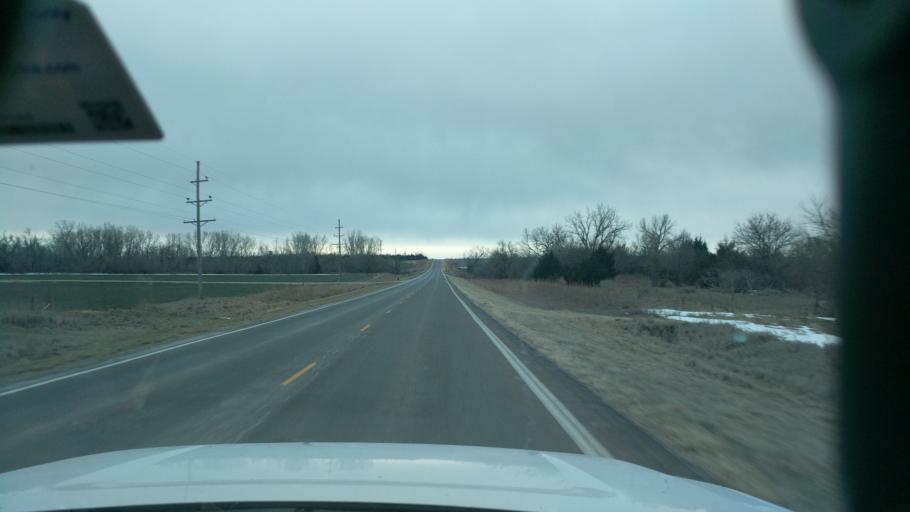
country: US
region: Kansas
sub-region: Marion County
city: Hillsboro
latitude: 38.3461
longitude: -97.3349
